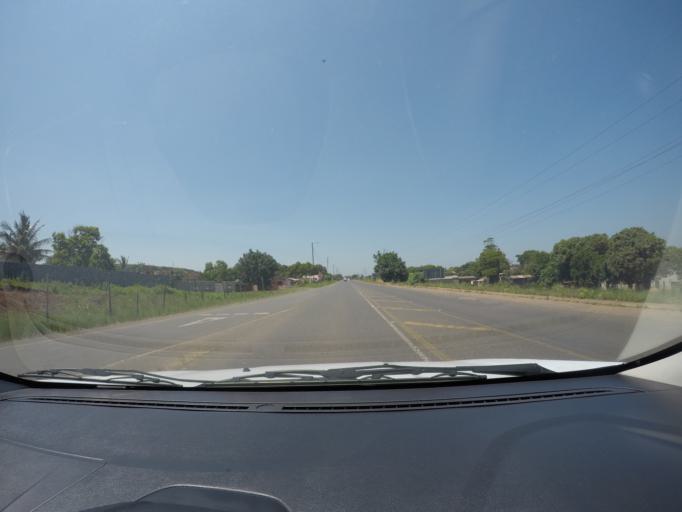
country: ZA
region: KwaZulu-Natal
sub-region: uThungulu District Municipality
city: eSikhawini
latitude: -28.8405
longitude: 31.9354
